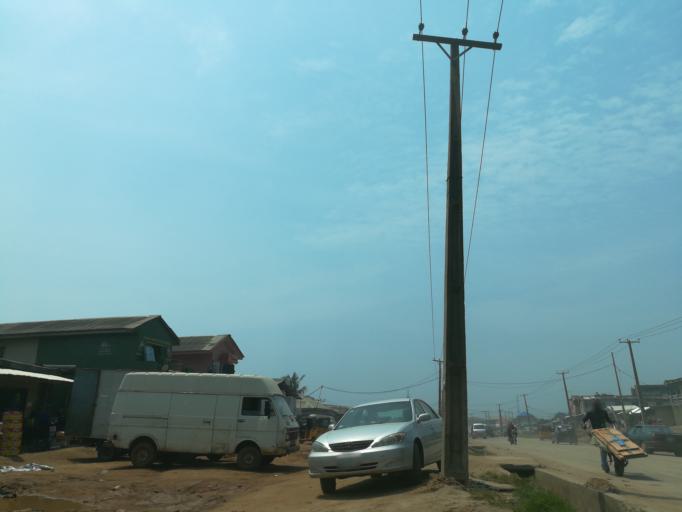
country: NG
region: Lagos
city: Ikorodu
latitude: 6.6304
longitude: 3.4834
